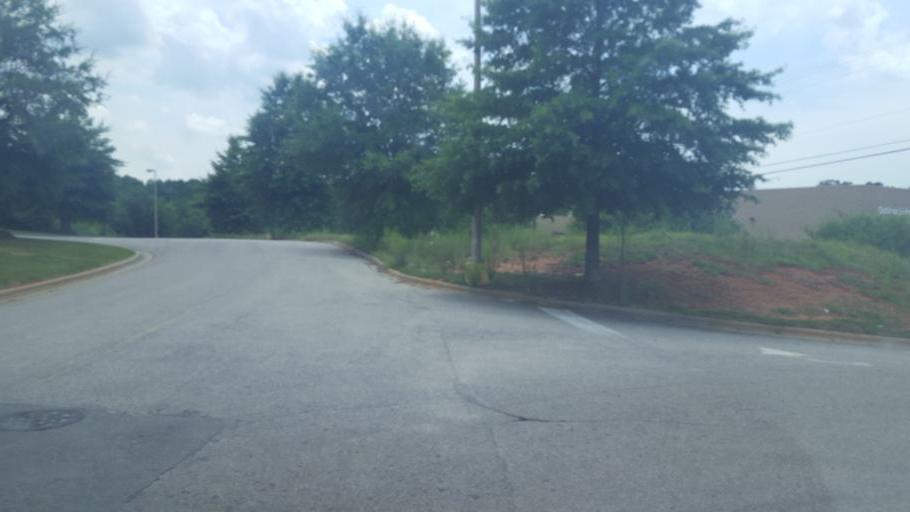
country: US
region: South Carolina
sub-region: York County
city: York
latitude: 34.9840
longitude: -81.2116
